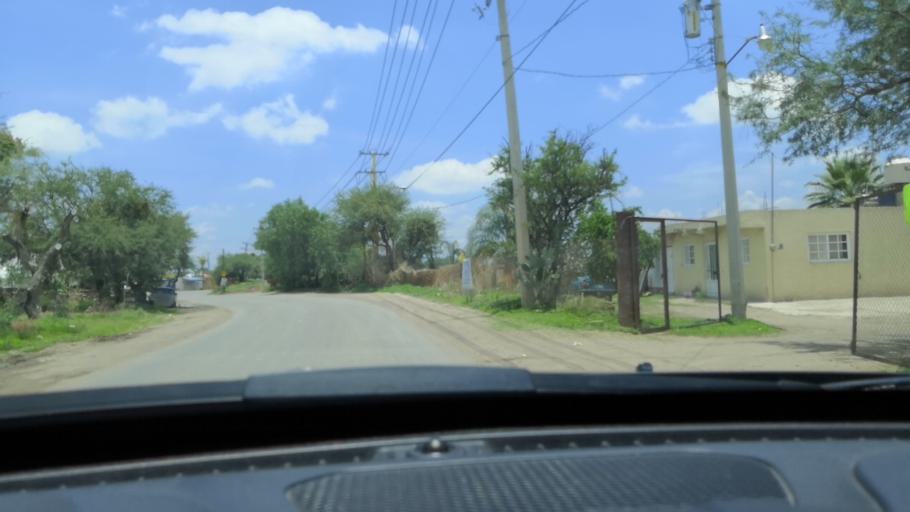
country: MX
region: Guanajuato
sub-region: Leon
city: Ladrilleras del Refugio
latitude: 21.0606
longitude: -101.5572
